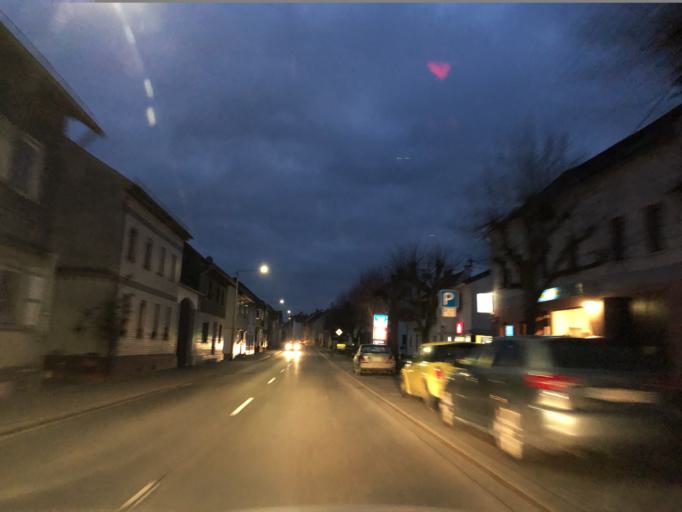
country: DE
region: Rheinland-Pfalz
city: Singhofen
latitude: 50.2733
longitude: 7.8355
